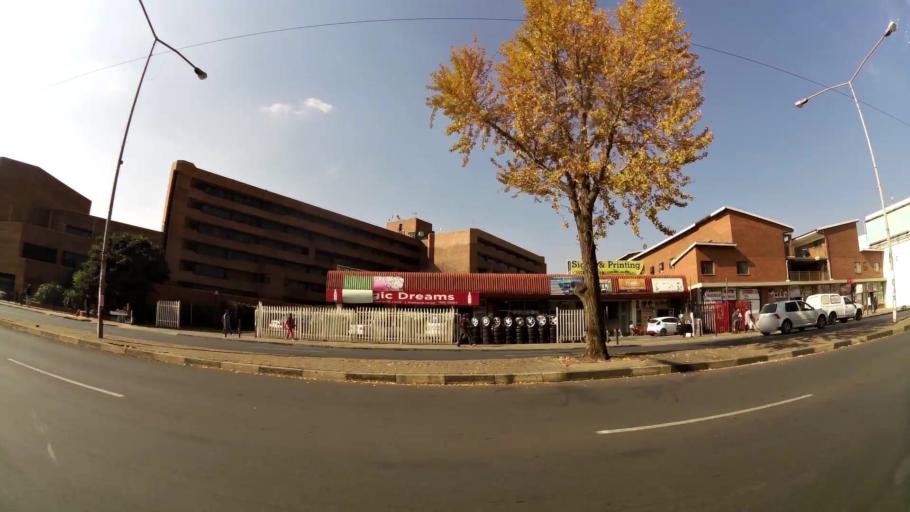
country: ZA
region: Gauteng
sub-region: City of Johannesburg Metropolitan Municipality
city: Modderfontein
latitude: -26.1028
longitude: 28.2264
